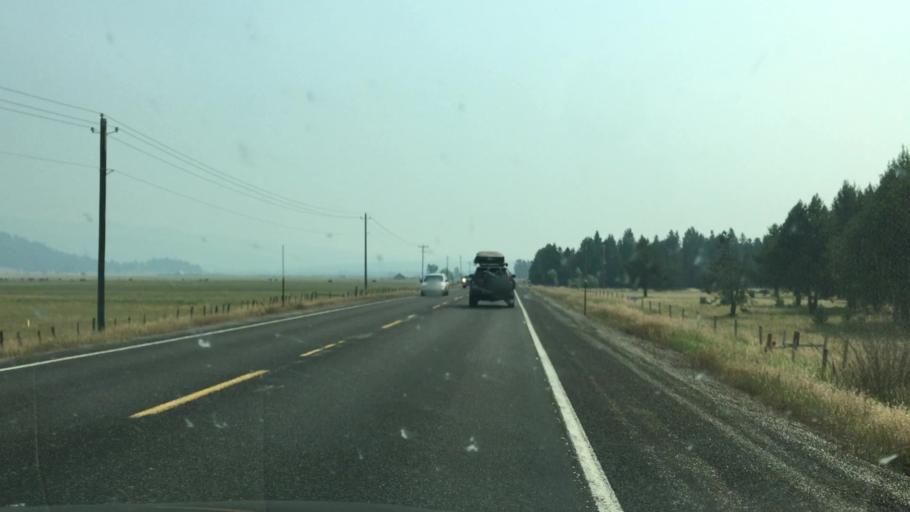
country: US
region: Idaho
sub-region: Valley County
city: Cascade
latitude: 44.4399
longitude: -115.9995
